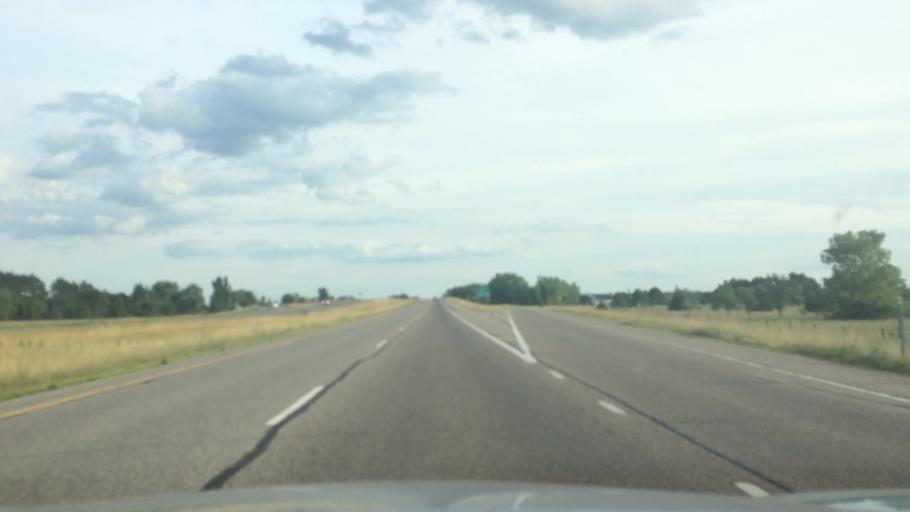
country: US
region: Wisconsin
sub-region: Portage County
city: Plover
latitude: 44.2188
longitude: -89.5248
